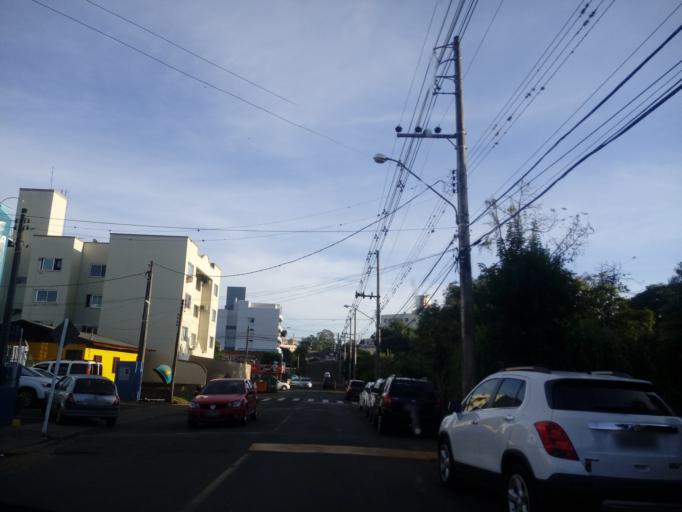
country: BR
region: Santa Catarina
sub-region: Chapeco
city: Chapeco
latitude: -27.0986
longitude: -52.6226
